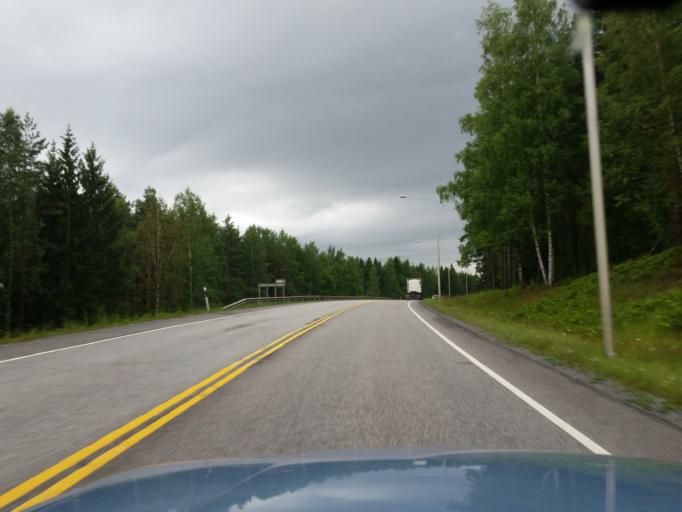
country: FI
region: Uusimaa
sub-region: Raaseporin
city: Ekenaes
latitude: 59.9761
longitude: 23.3972
